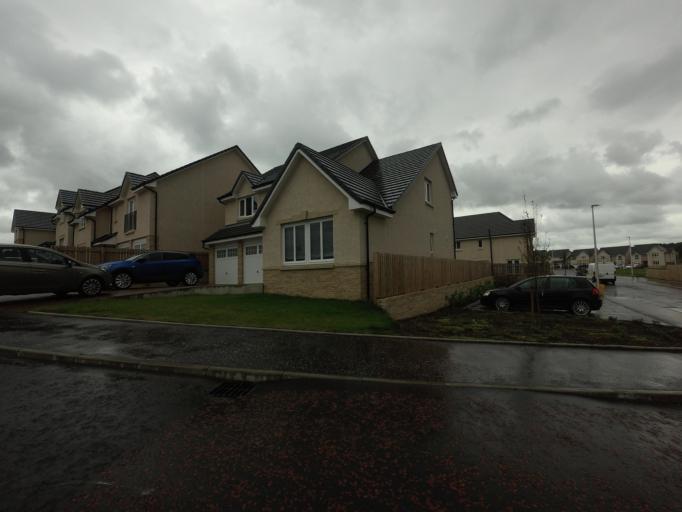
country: GB
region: Scotland
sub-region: West Lothian
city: West Calder
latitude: 55.8575
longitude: -3.5756
